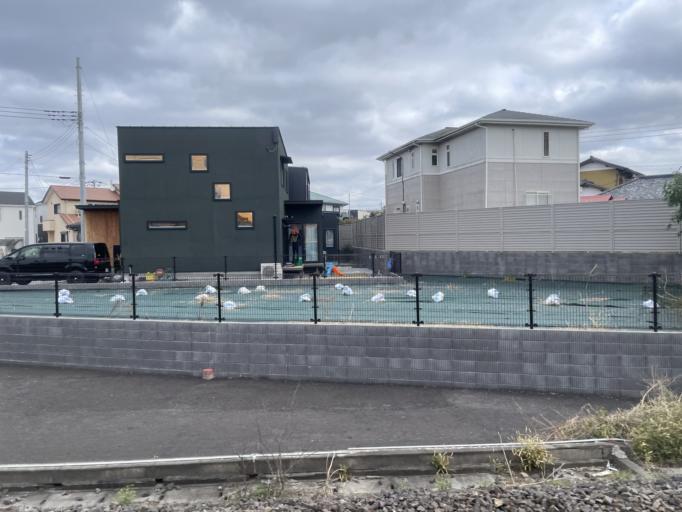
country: JP
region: Chiba
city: Narita
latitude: 35.7601
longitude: 140.3075
